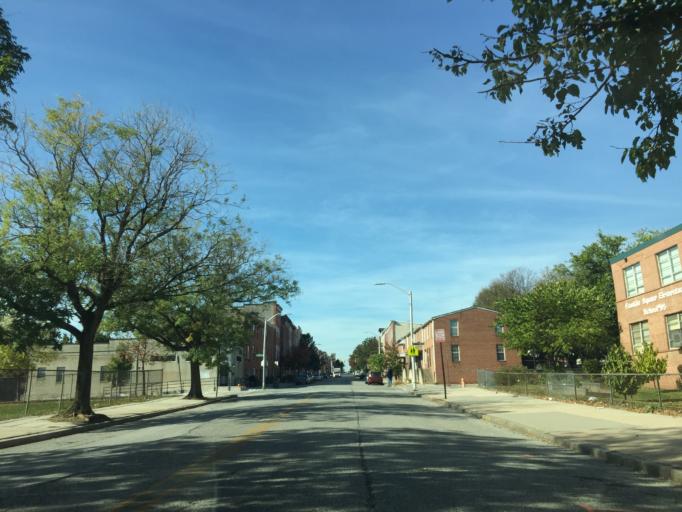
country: US
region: Maryland
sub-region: City of Baltimore
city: Baltimore
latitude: 39.2908
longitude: -76.6405
